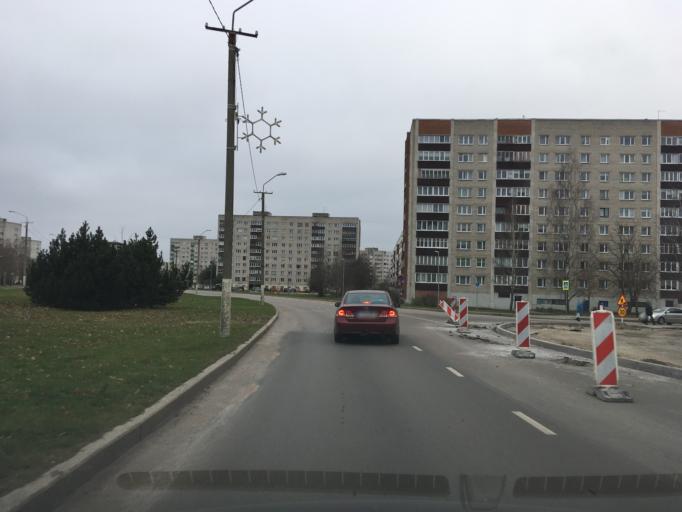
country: EE
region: Ida-Virumaa
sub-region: Narva linn
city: Narva
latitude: 59.3823
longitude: 28.1800
